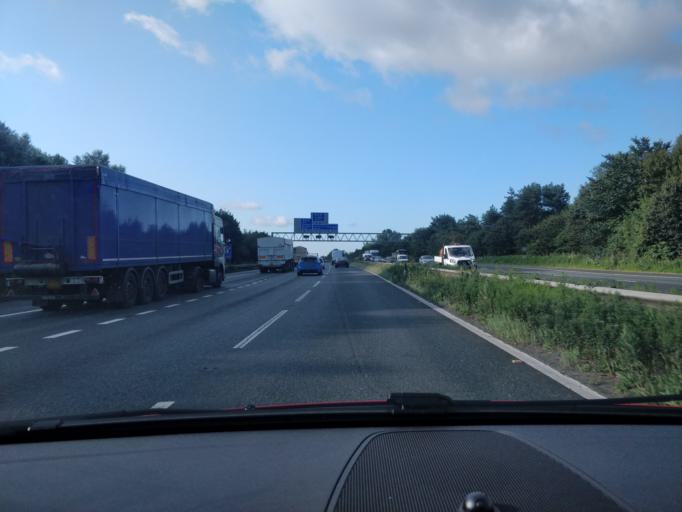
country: GB
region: England
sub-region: Knowsley
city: Prescot
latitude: 53.4091
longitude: -2.8138
